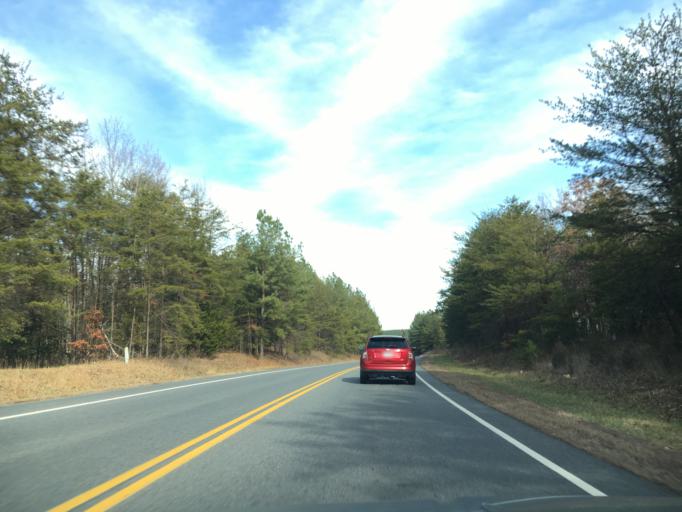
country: US
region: Virginia
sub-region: Louisa County
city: Louisa
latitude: 38.0593
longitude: -77.8809
